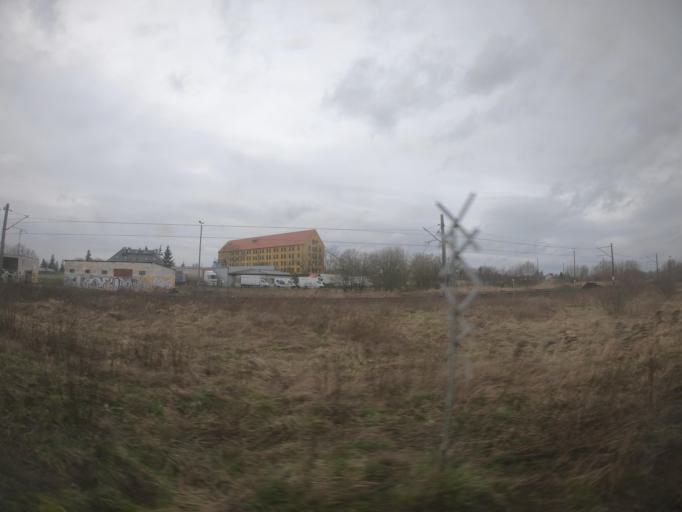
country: PL
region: West Pomeranian Voivodeship
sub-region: Powiat szczecinecki
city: Szczecinek
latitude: 53.7005
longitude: 16.7166
